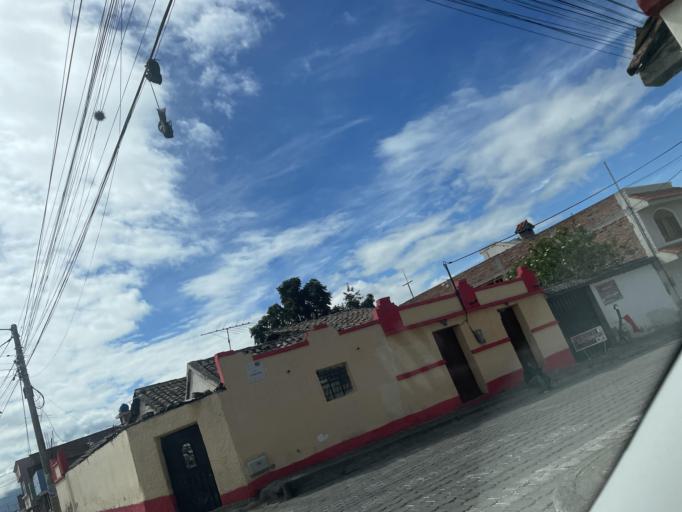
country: EC
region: Chimborazo
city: Guano
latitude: -1.6036
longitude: -78.6447
